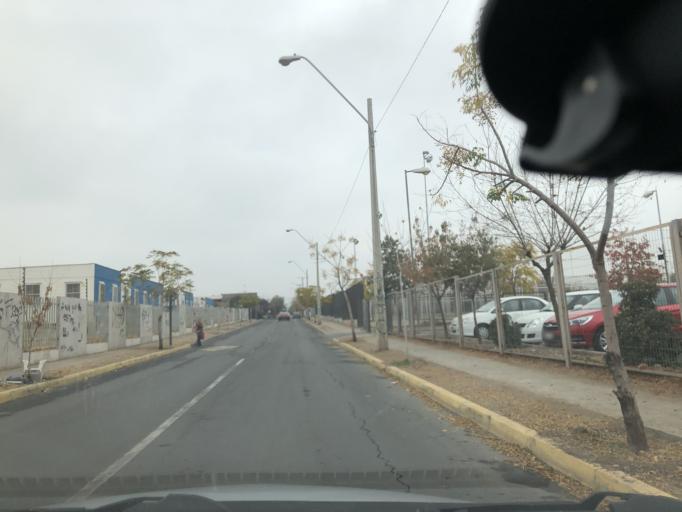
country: CL
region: Santiago Metropolitan
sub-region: Provincia de Cordillera
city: Puente Alto
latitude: -33.5908
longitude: -70.5953
